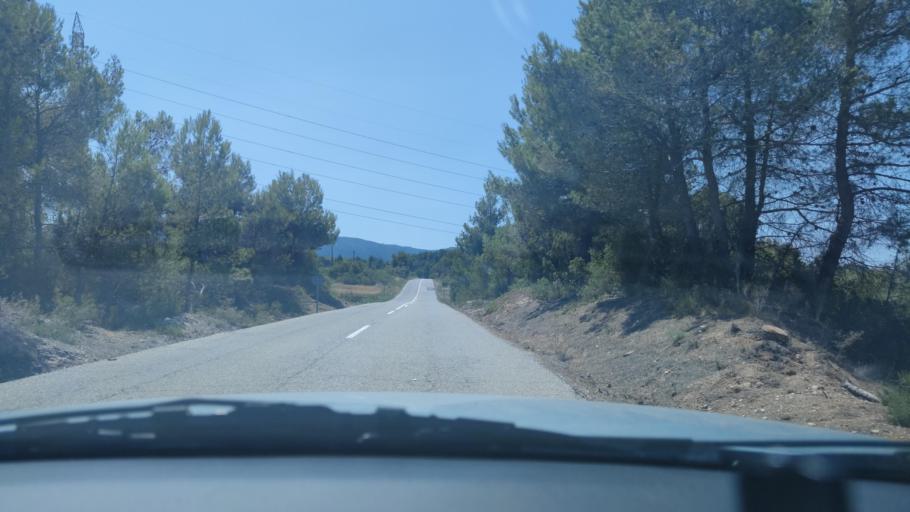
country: ES
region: Catalonia
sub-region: Provincia de Tarragona
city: Vallclara
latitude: 41.3979
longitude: 0.9546
